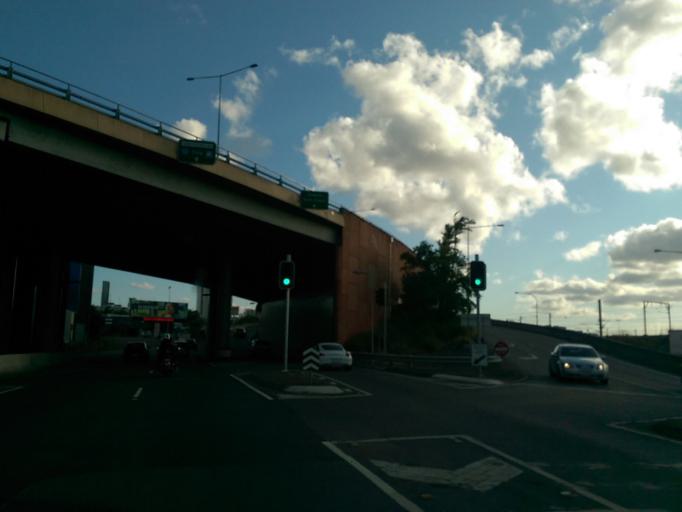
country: AU
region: Queensland
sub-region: Brisbane
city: Windsor
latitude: -27.4396
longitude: 153.0403
